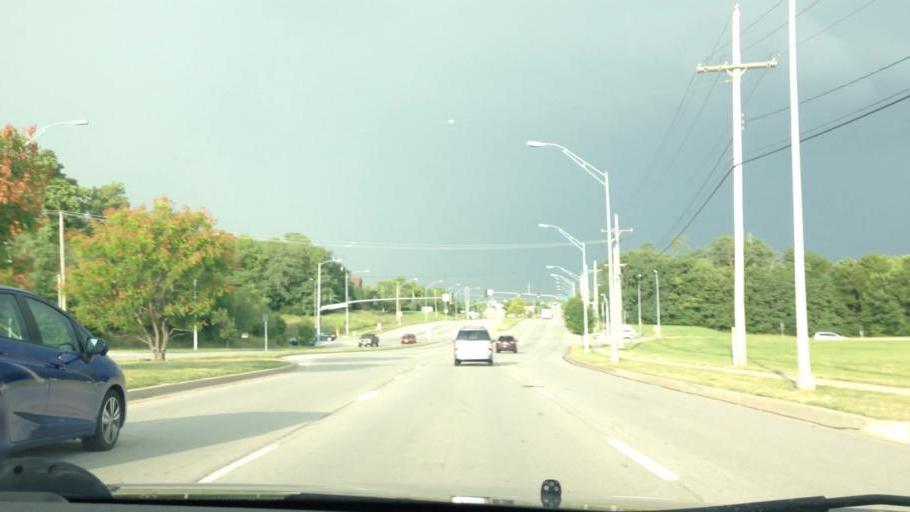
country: US
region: Missouri
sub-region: Clay County
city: Gladstone
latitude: 39.2463
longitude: -94.6028
